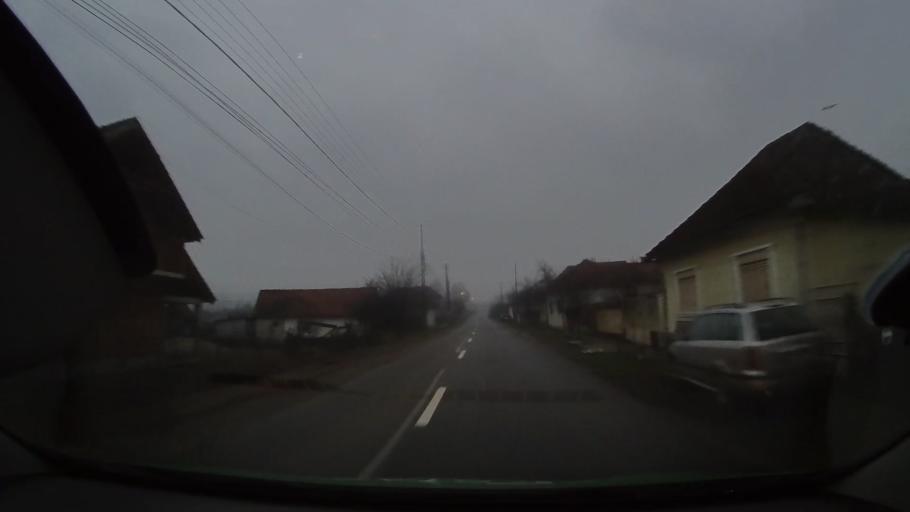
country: RO
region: Arad
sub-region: Comuna Beliu
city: Beliu
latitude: 46.4871
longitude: 21.9933
